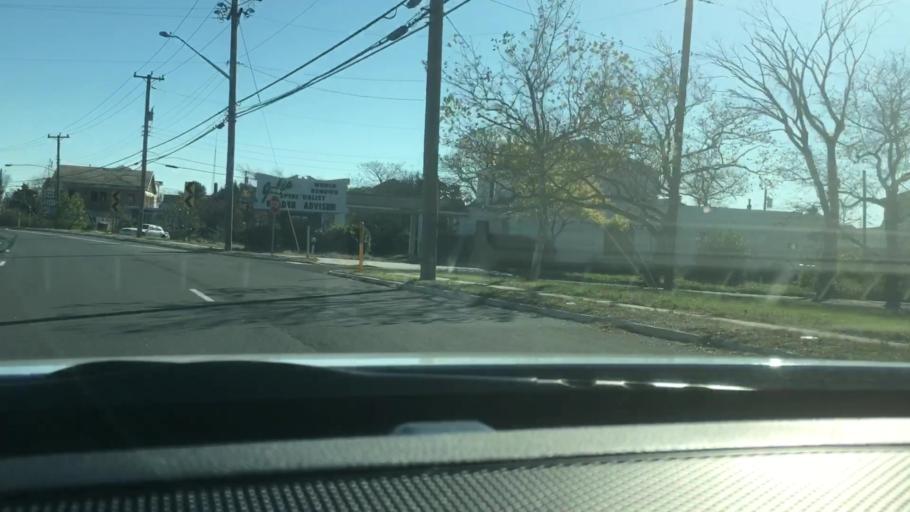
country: US
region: New Jersey
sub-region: Atlantic County
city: Pleasantville
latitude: 39.3862
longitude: -74.5139
